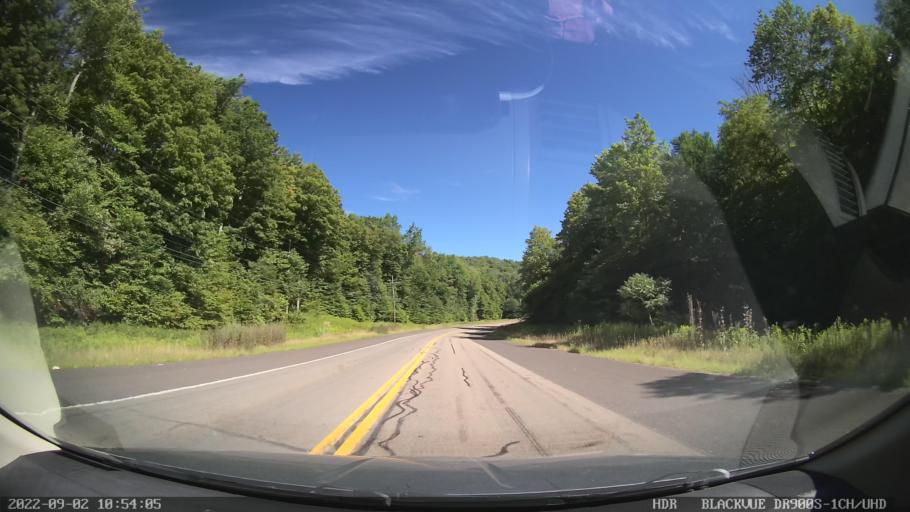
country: US
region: Pennsylvania
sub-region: Tioga County
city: Blossburg
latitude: 41.6549
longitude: -77.0946
